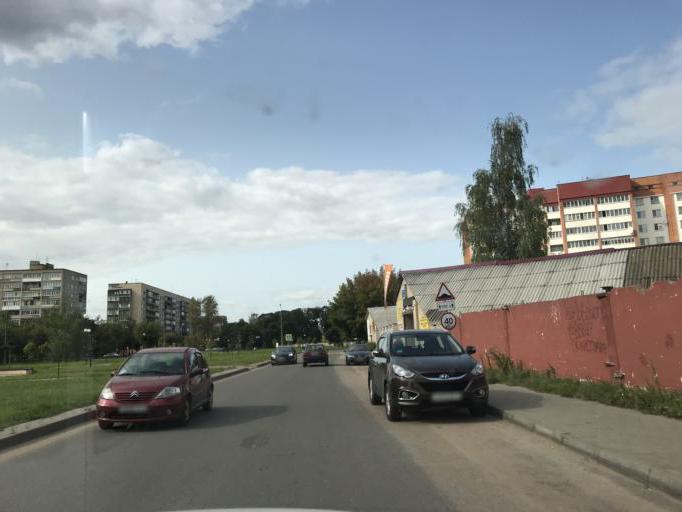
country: BY
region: Mogilev
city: Mahilyow
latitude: 53.8776
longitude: 30.3275
